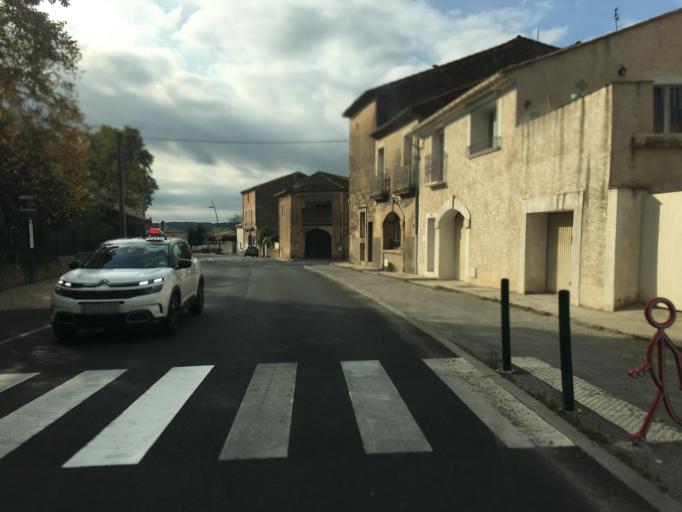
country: FR
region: Languedoc-Roussillon
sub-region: Departement de l'Herault
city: Nebian
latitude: 43.6064
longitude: 3.4360
